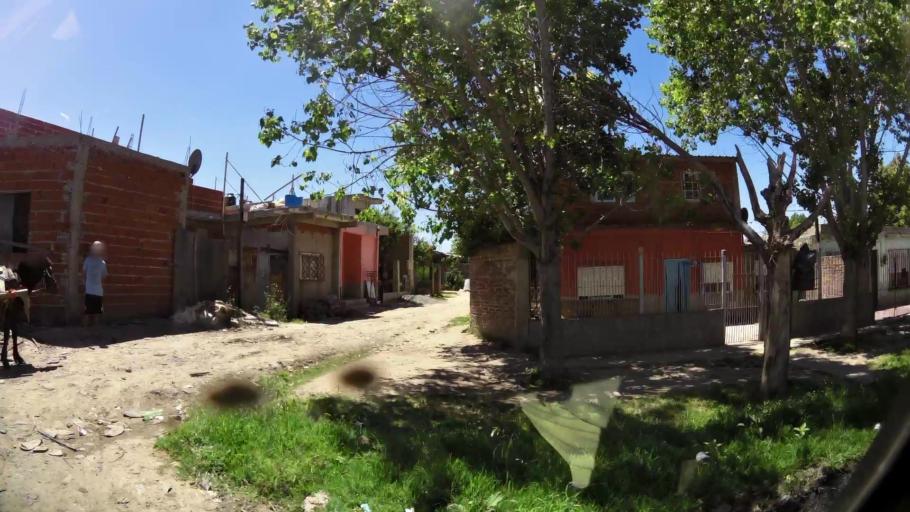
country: AR
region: Buenos Aires
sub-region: Partido de Quilmes
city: Quilmes
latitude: -34.7233
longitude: -58.3254
